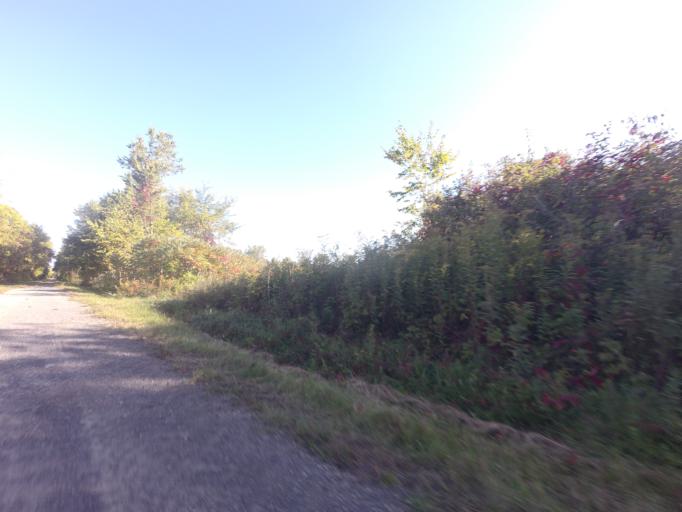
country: CA
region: Ontario
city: Hawkesbury
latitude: 45.5239
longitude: -74.5439
